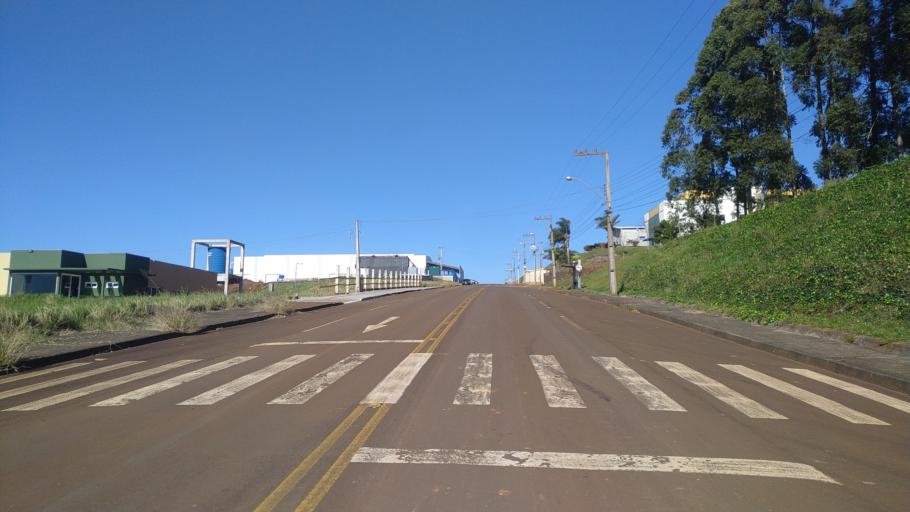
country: BR
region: Santa Catarina
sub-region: Chapeco
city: Chapeco
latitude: -27.1552
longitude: -52.6023
